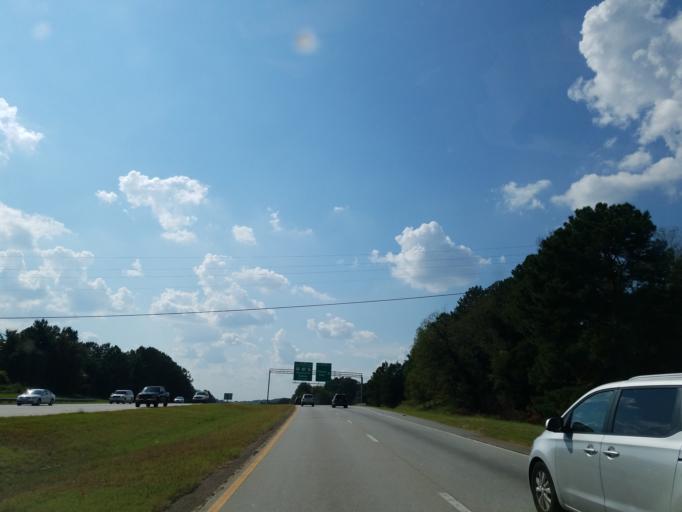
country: US
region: Georgia
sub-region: Clarke County
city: Athens
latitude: 33.9165
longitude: -83.3975
